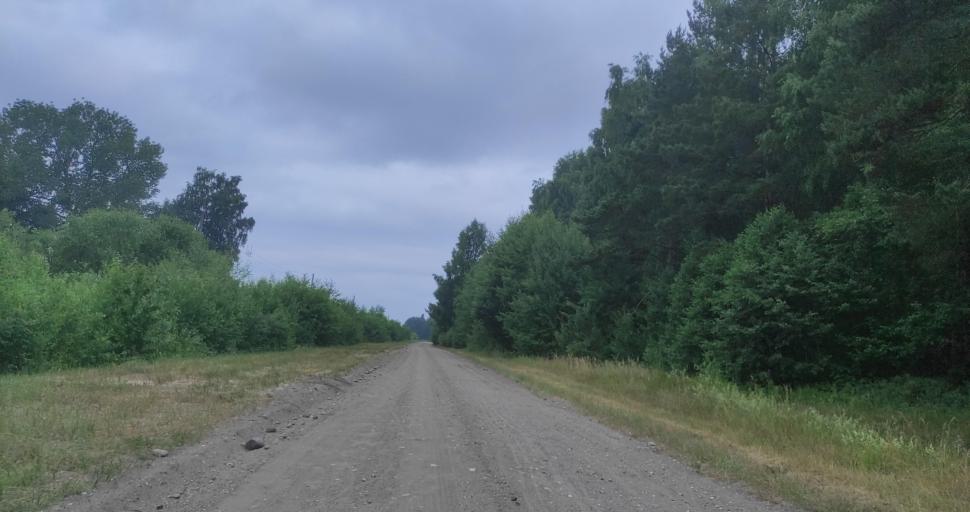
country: LV
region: Pavilostas
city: Pavilosta
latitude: 56.8859
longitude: 21.2032
